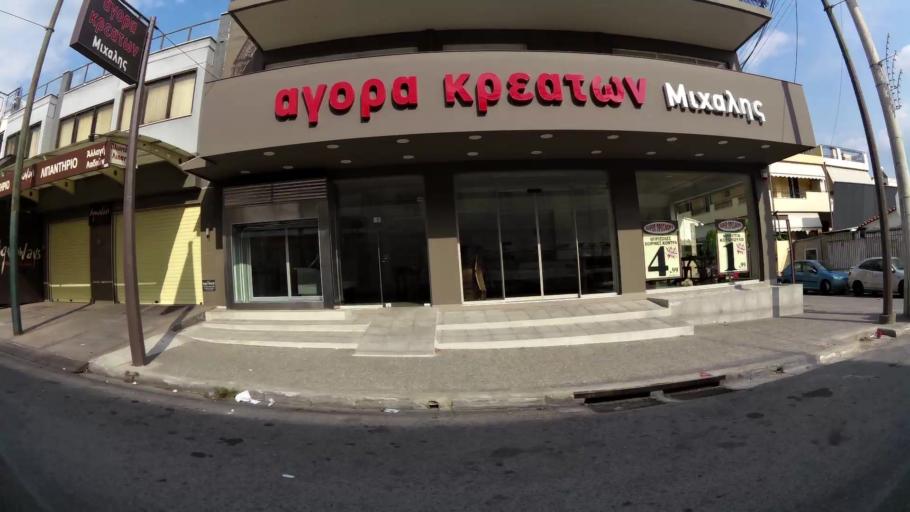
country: GR
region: Attica
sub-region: Nomarchia Athinas
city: Ilion
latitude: 38.0403
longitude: 23.7038
